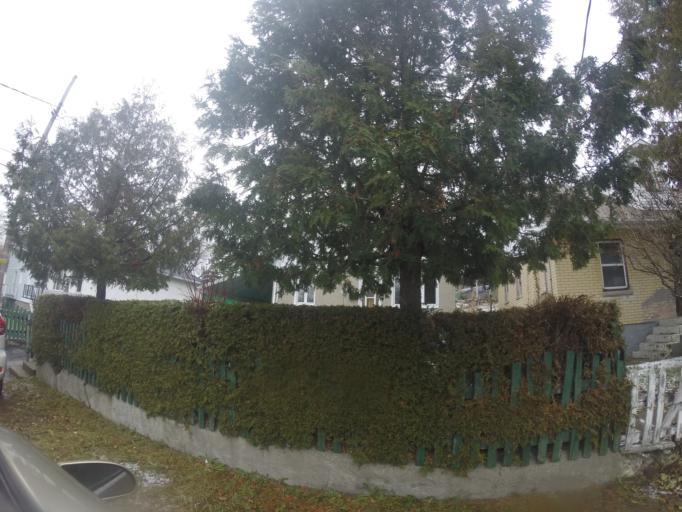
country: CA
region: Ontario
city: Greater Sudbury
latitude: 46.4968
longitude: -81.0096
